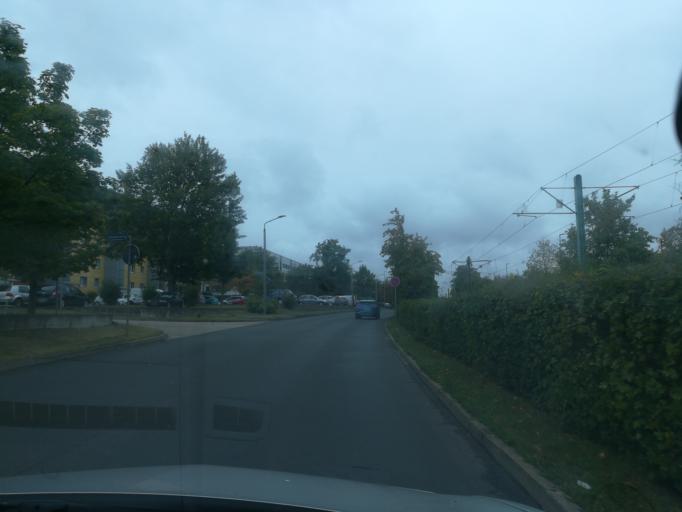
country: DE
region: Saxony-Anhalt
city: Diesdorf
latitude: 52.1499
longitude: 11.5857
